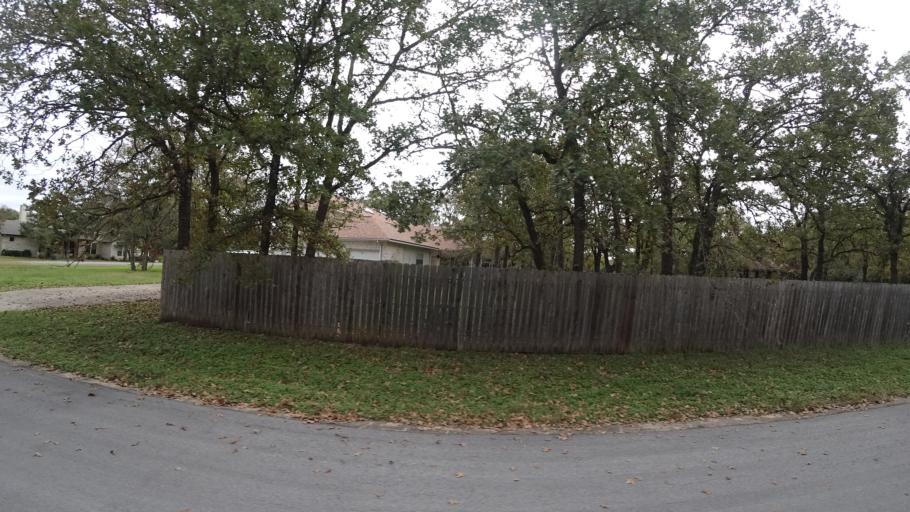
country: US
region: Texas
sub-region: Travis County
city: Shady Hollow
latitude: 30.1409
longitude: -97.8836
